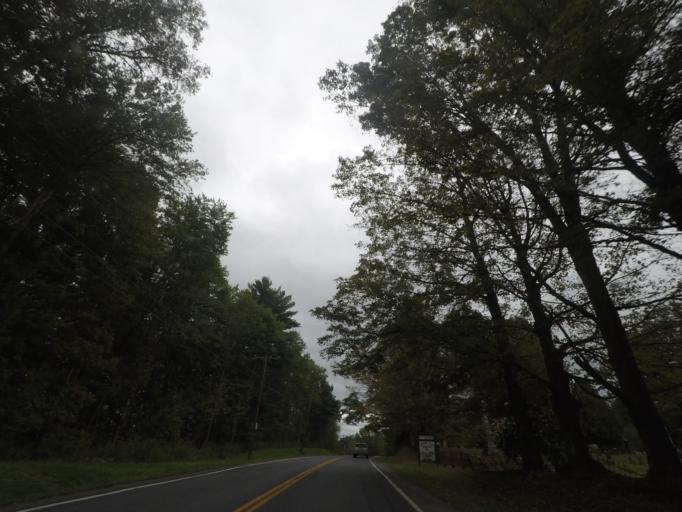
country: US
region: New York
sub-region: Washington County
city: Cambridge
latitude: 42.9533
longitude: -73.4293
